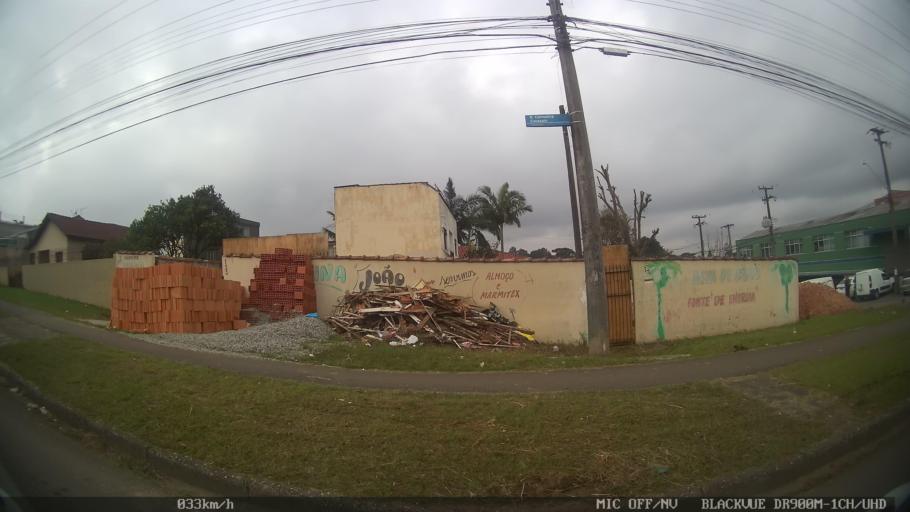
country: BR
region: Parana
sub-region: Almirante Tamandare
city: Almirante Tamandare
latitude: -25.3655
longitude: -49.2628
